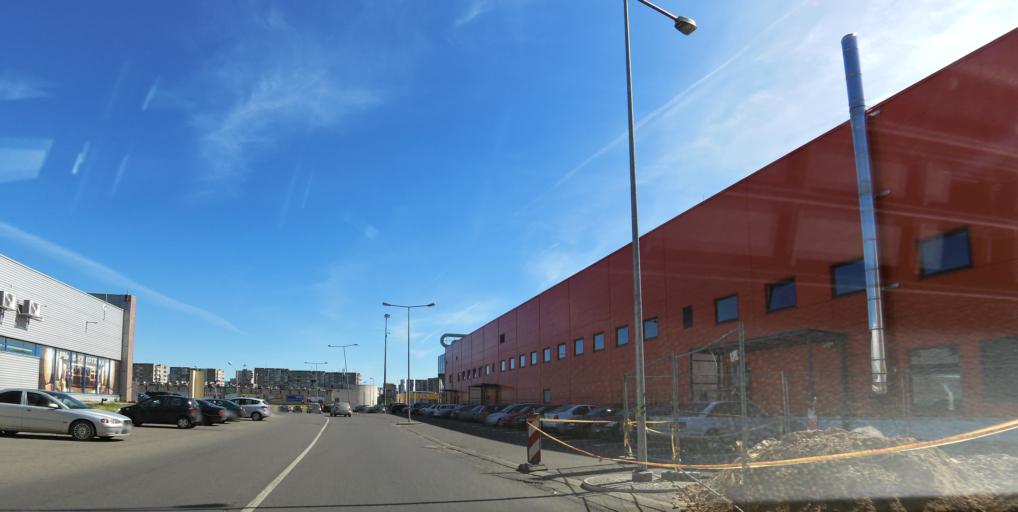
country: LT
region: Vilnius County
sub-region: Vilnius
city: Fabijoniskes
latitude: 54.7224
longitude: 25.2410
